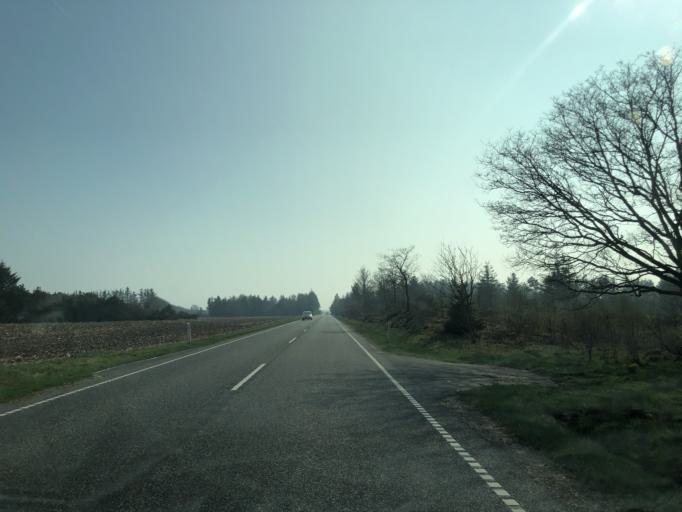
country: DK
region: Central Jutland
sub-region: Ringkobing-Skjern Kommune
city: Skjern
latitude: 55.8720
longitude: 8.3929
